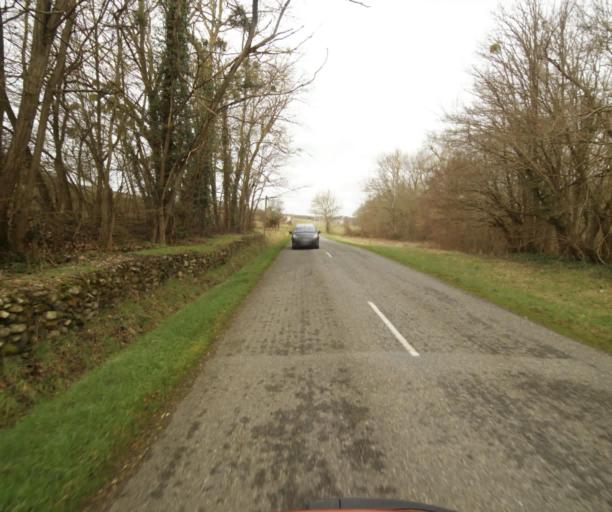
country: FR
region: Midi-Pyrenees
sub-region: Departement de l'Ariege
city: Pamiers
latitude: 43.1342
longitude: 1.5418
